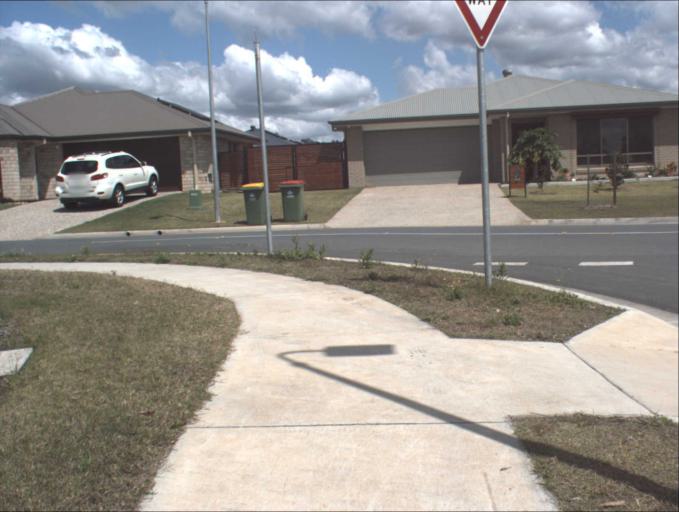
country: AU
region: Queensland
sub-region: Logan
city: Chambers Flat
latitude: -27.7989
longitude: 153.1085
